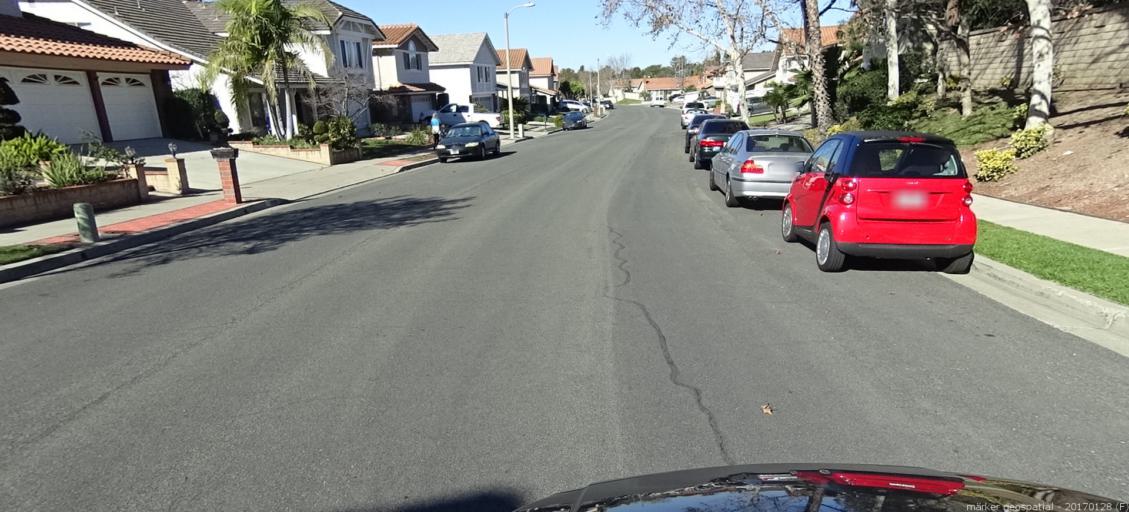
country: US
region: California
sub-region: Orange County
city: Lake Forest
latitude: 33.6576
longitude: -117.6920
